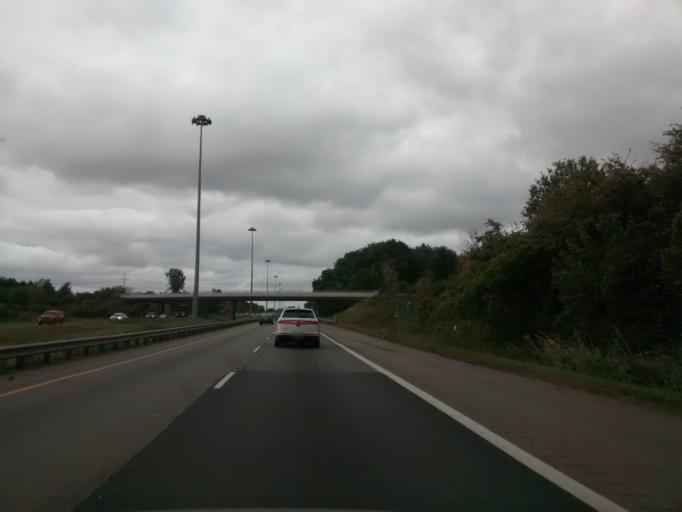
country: CA
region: Ontario
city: Ancaster
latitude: 43.2216
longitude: -79.9605
